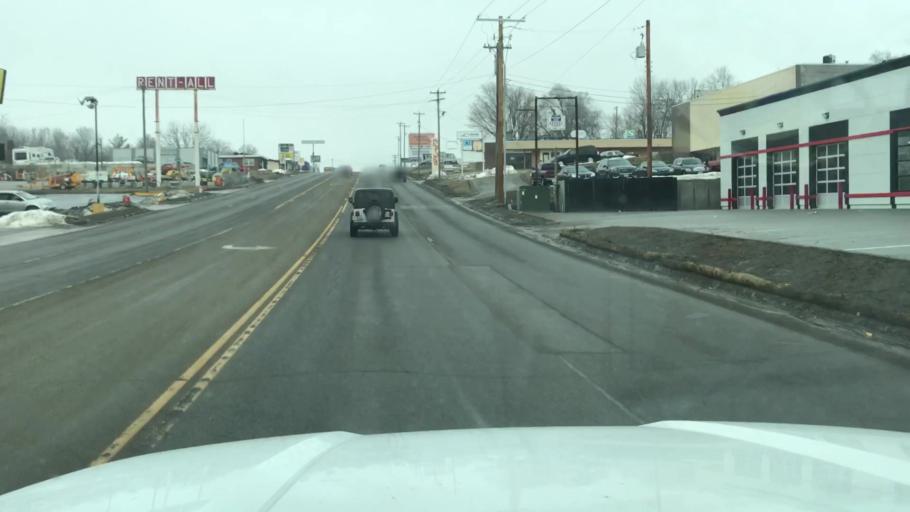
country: US
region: Missouri
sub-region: Buchanan County
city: Saint Joseph
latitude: 39.7627
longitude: -94.8037
